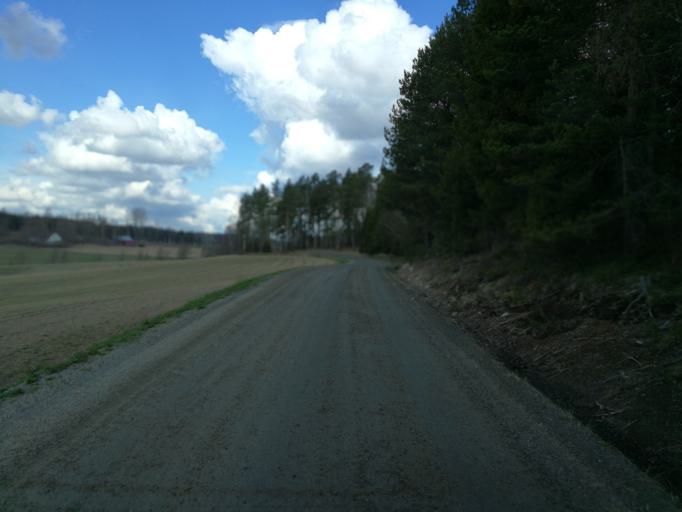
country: FI
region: Uusimaa
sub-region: Raaseporin
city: Inga
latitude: 60.1188
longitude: 24.0319
